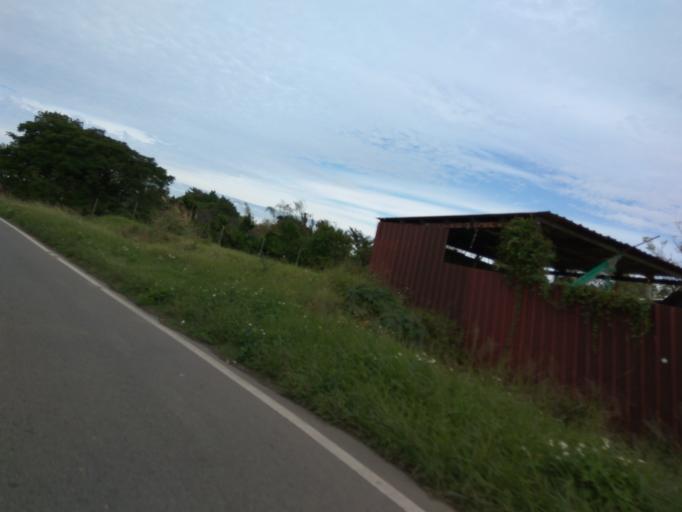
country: TW
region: Taiwan
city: Daxi
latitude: 24.9473
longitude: 121.1442
